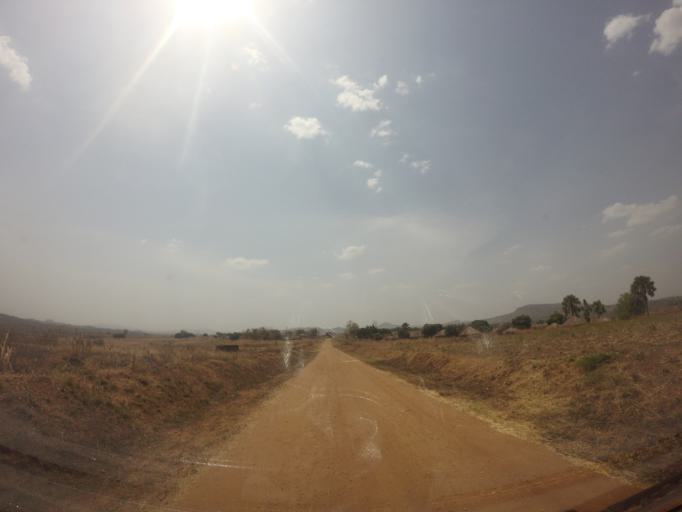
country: UG
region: Northern Region
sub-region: Arua District
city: Arua
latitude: 2.9085
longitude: 31.0586
